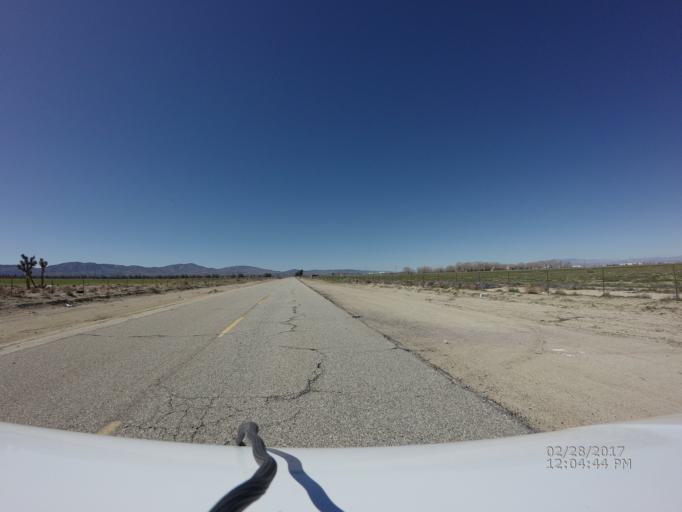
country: US
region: California
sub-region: Los Angeles County
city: Palmdale
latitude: 34.5948
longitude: -118.0522
